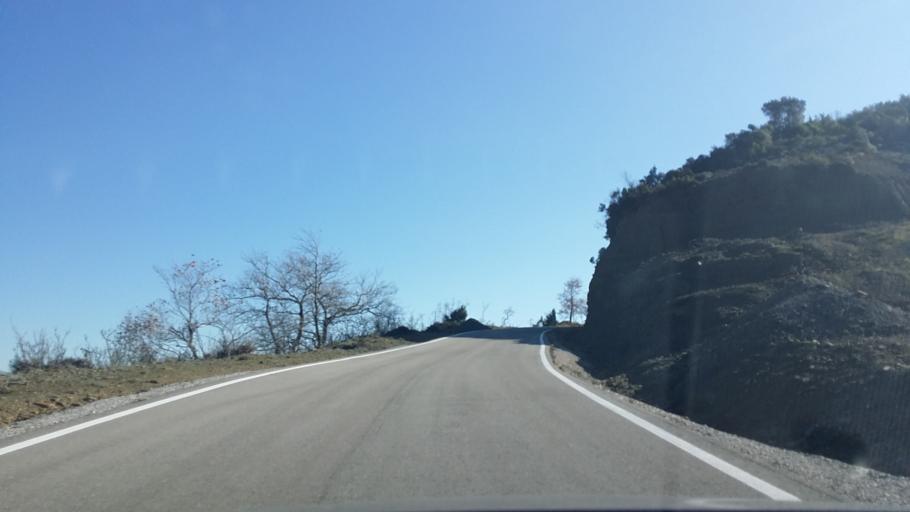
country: GR
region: West Greece
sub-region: Nomos Aitolias kai Akarnanias
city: Krikellos
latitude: 38.9900
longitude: 21.2773
